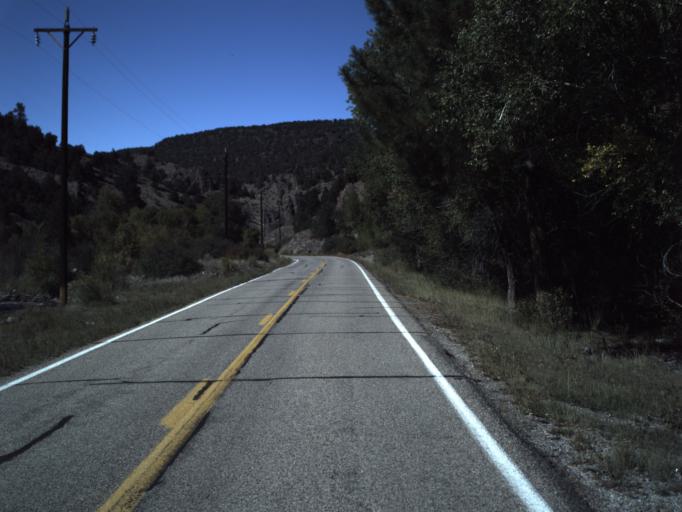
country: US
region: Utah
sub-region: Beaver County
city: Beaver
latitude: 38.2679
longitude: -112.5493
